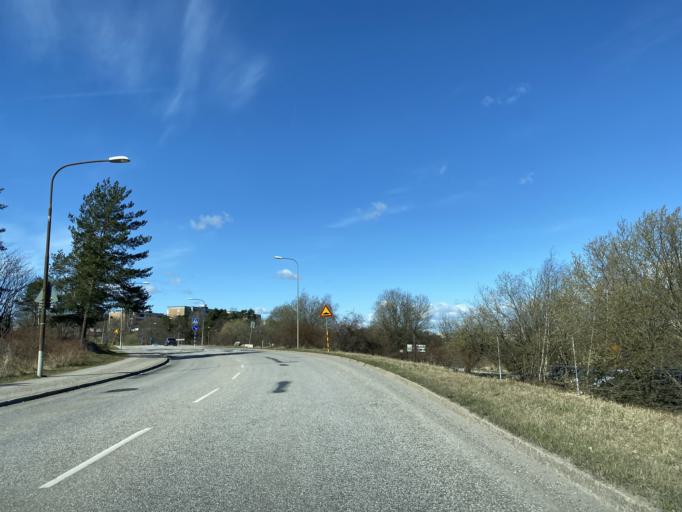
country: SE
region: Stockholm
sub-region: Stockholms Kommun
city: Arsta
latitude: 59.2883
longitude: 18.0414
